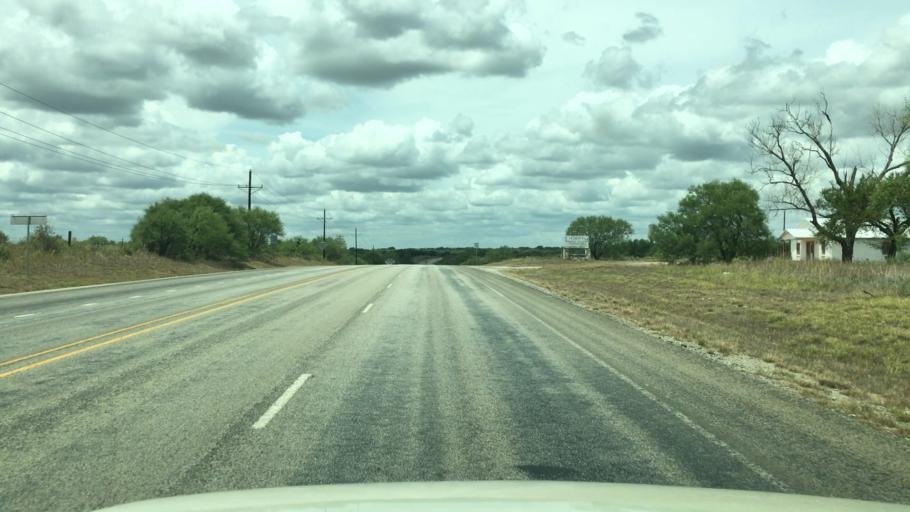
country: US
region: Texas
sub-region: McCulloch County
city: Brady
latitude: 31.0031
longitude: -99.1881
